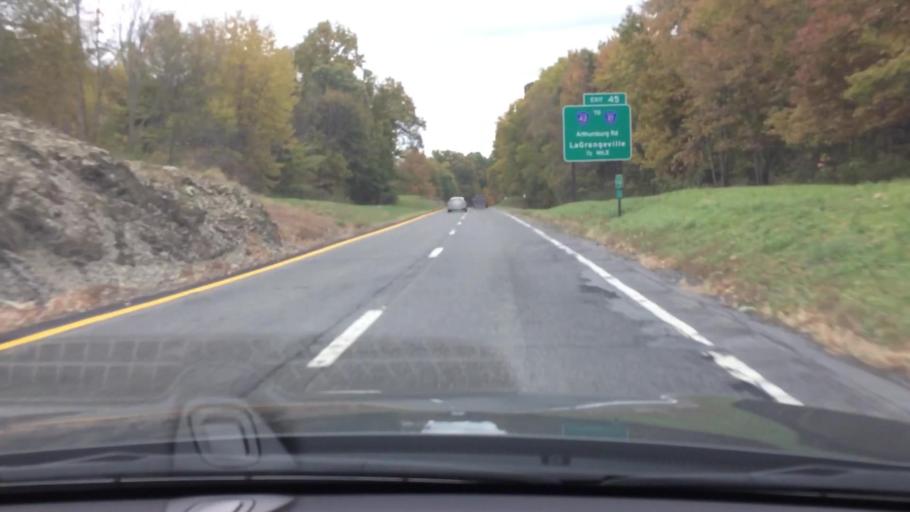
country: US
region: New York
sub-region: Dutchess County
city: Hillside Lake
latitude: 41.6405
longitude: -73.7863
